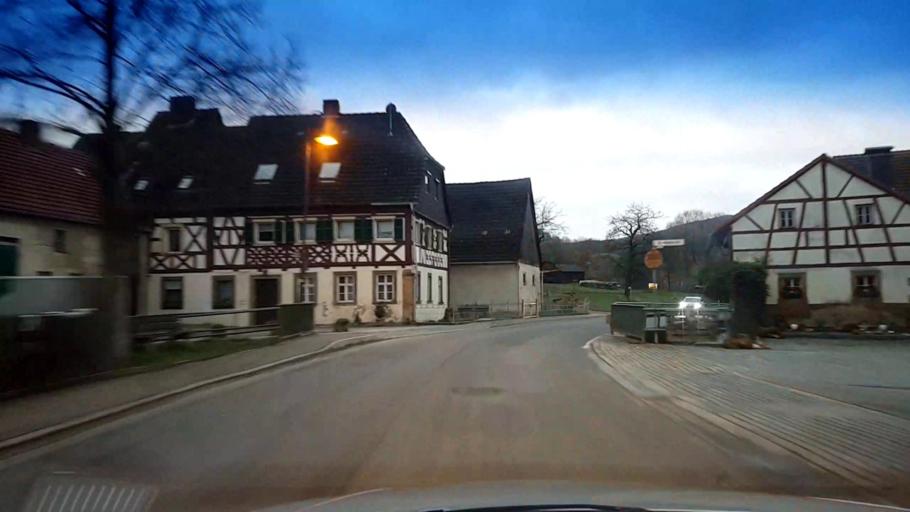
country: DE
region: Bavaria
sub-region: Upper Franconia
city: Schesslitz
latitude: 50.0103
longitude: 11.0738
